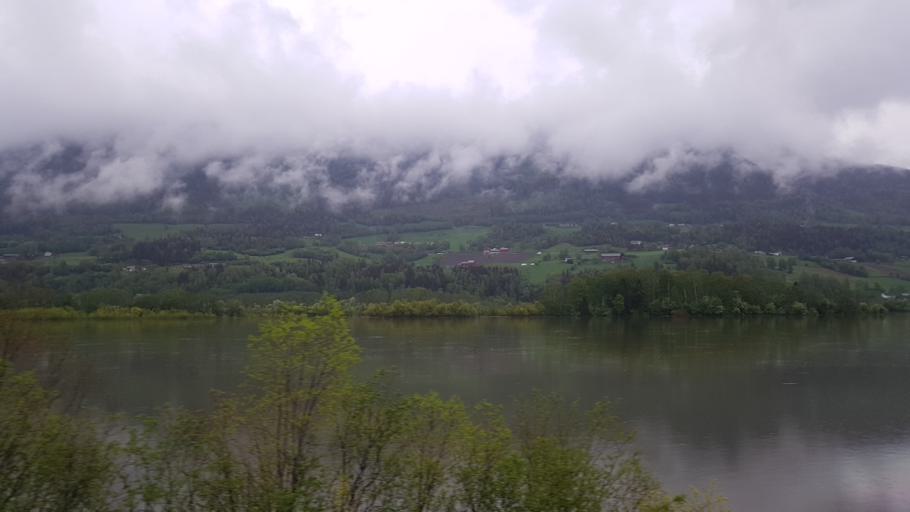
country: NO
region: Oppland
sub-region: Oyer
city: Tretten
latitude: 61.3911
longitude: 10.2534
